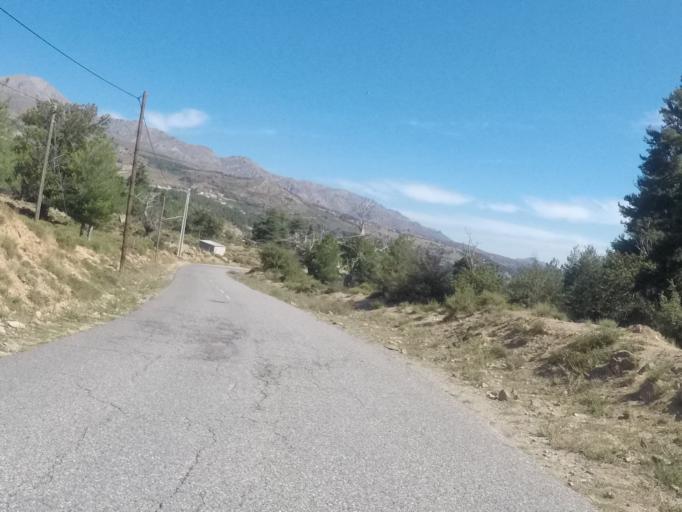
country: FR
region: Corsica
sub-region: Departement de la Haute-Corse
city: Corte
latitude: 42.3141
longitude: 8.9698
